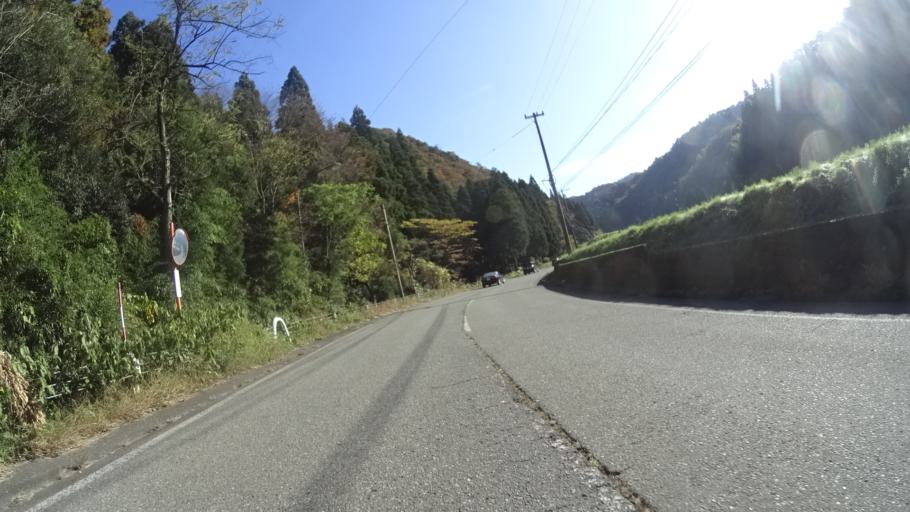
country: JP
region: Ishikawa
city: Komatsu
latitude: 36.3724
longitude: 136.5546
